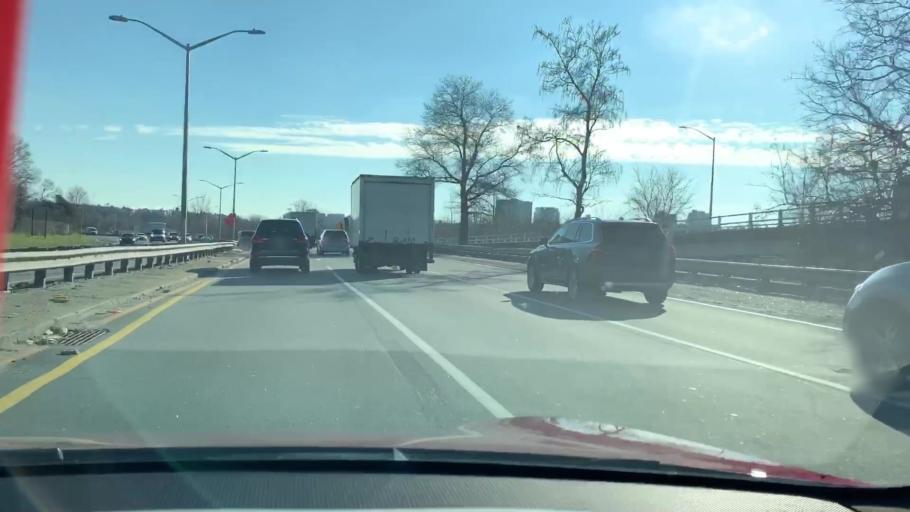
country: US
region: New York
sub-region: Queens County
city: Jamaica
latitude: 40.7275
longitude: -73.8327
